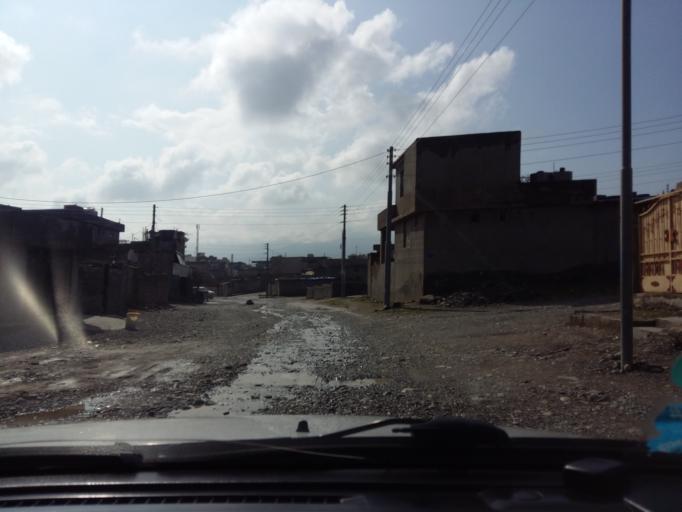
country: IQ
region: As Sulaymaniyah
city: Qeladize
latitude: 36.1929
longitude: 45.1231
